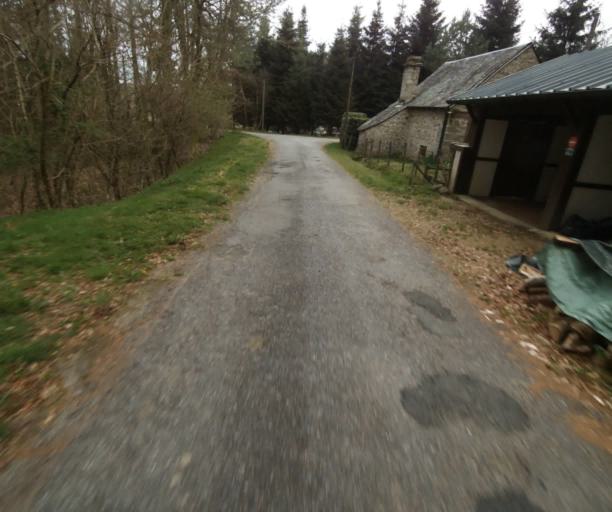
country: FR
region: Limousin
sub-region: Departement de la Correze
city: Argentat
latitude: 45.2211
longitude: 1.9663
